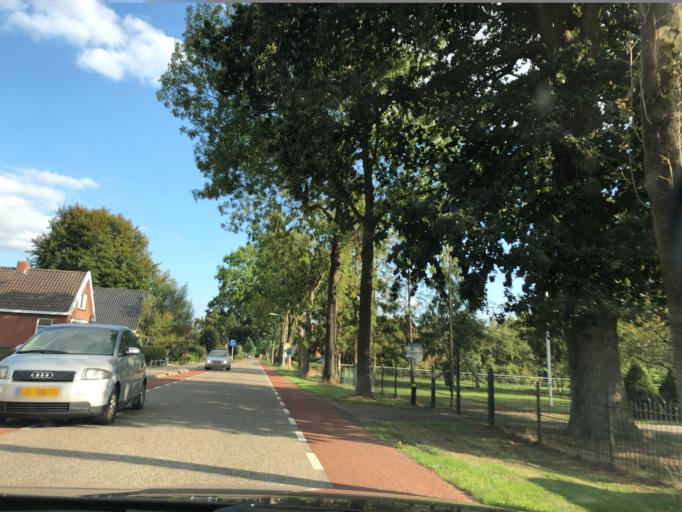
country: NL
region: Groningen
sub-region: Gemeente Vlagtwedde
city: Sellingen
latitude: 53.0124
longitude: 7.1814
